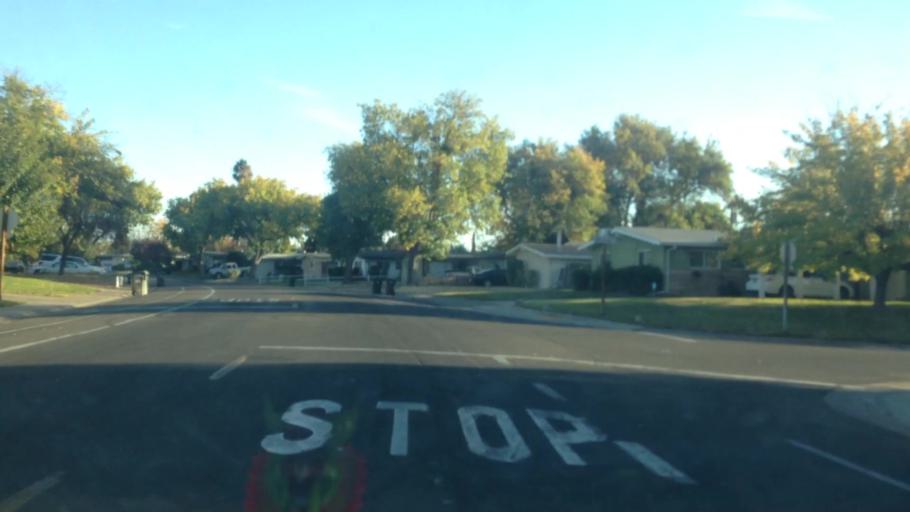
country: US
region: California
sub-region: Sacramento County
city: North Highlands
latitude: 38.6881
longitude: -121.3696
